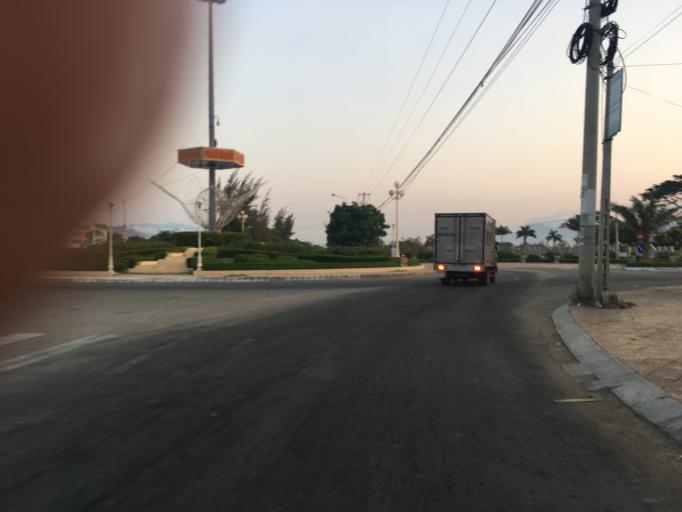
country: VN
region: Ninh Thuan
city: Phan Rang-Thap Cham
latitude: 11.5625
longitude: 109.0216
